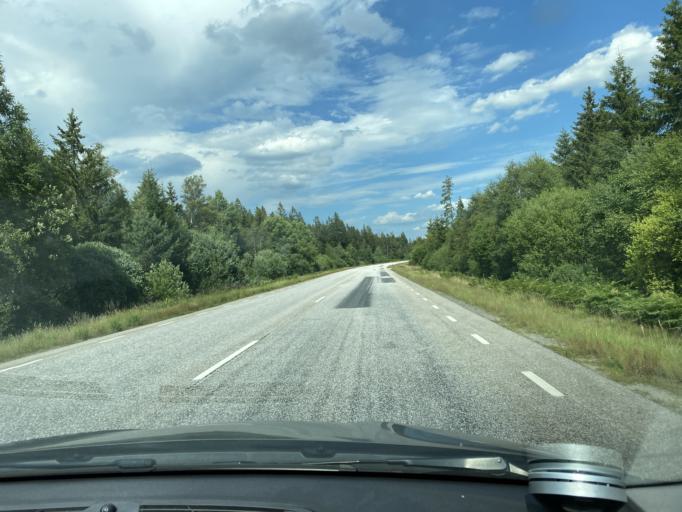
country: SE
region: Kronoberg
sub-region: Markaryds Kommun
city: Markaryd
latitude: 56.4234
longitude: 13.5525
